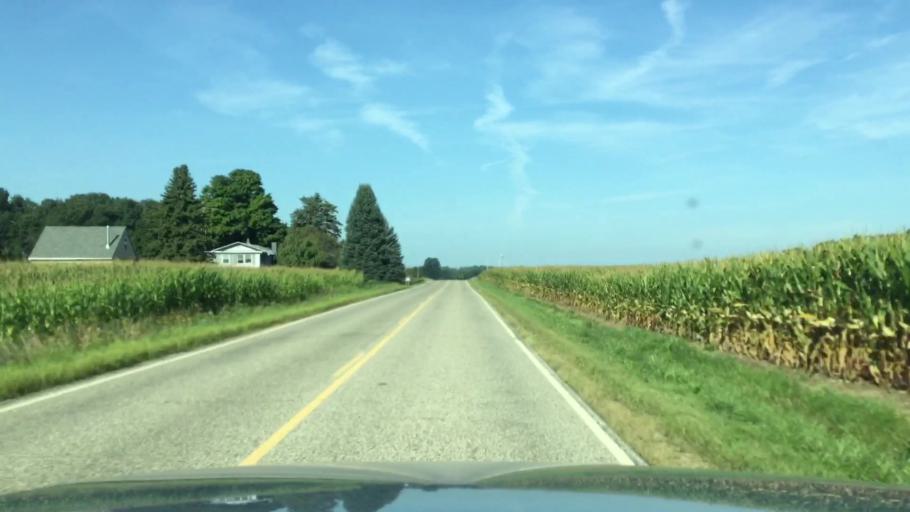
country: US
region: Michigan
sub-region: Lenawee County
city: Hudson
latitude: 41.9277
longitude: -84.3874
